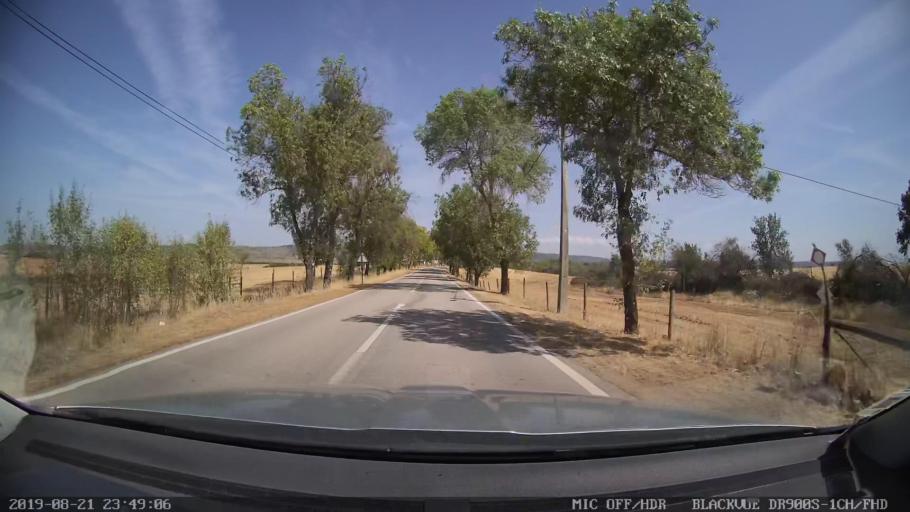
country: PT
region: Castelo Branco
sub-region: Idanha-A-Nova
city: Idanha-a-Nova
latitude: 39.8737
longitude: -7.2517
